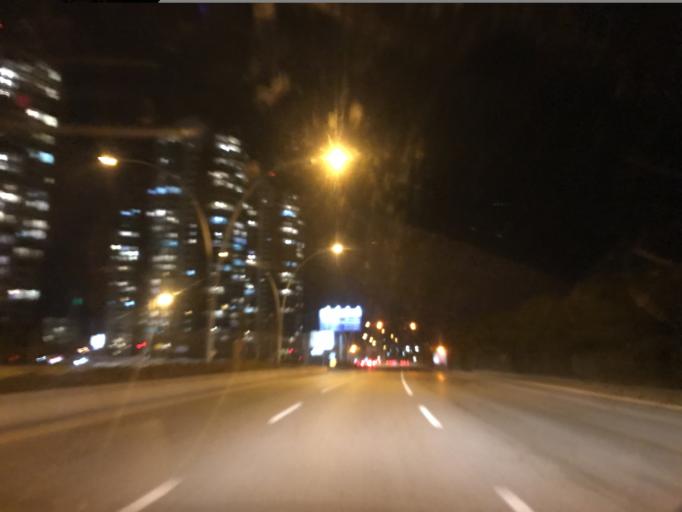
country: TR
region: Ankara
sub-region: Goelbasi
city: Golbasi
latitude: 39.8448
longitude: 32.8282
